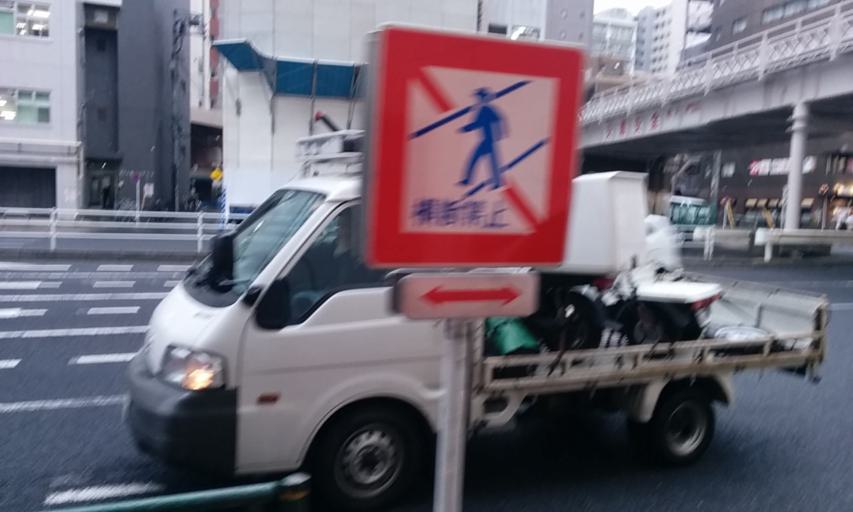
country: JP
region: Tokyo
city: Tokyo
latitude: 35.7078
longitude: 139.7539
